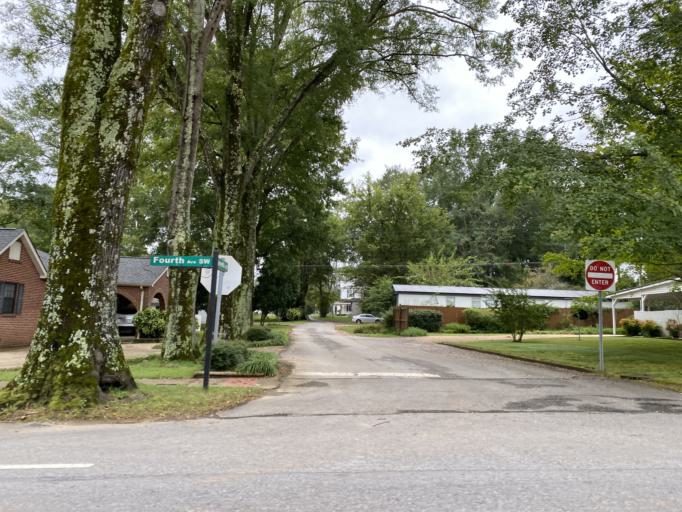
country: US
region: Alabama
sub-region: Franklin County
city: Red Bay
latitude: 34.4427
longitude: -88.1519
